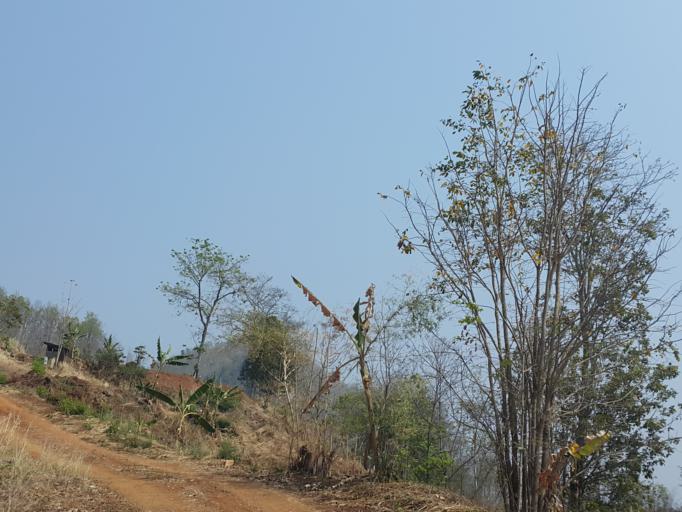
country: TH
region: Chiang Mai
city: Mae On
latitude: 18.7773
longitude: 99.2362
